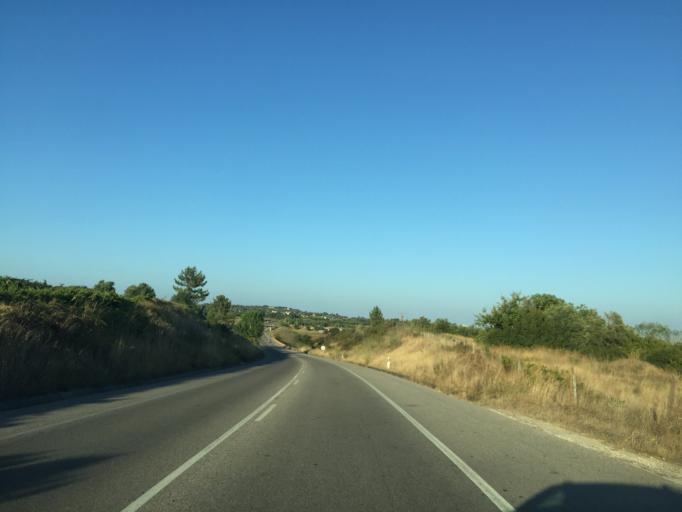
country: PT
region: Santarem
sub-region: Cartaxo
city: Pontevel
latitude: 39.1559
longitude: -8.8574
